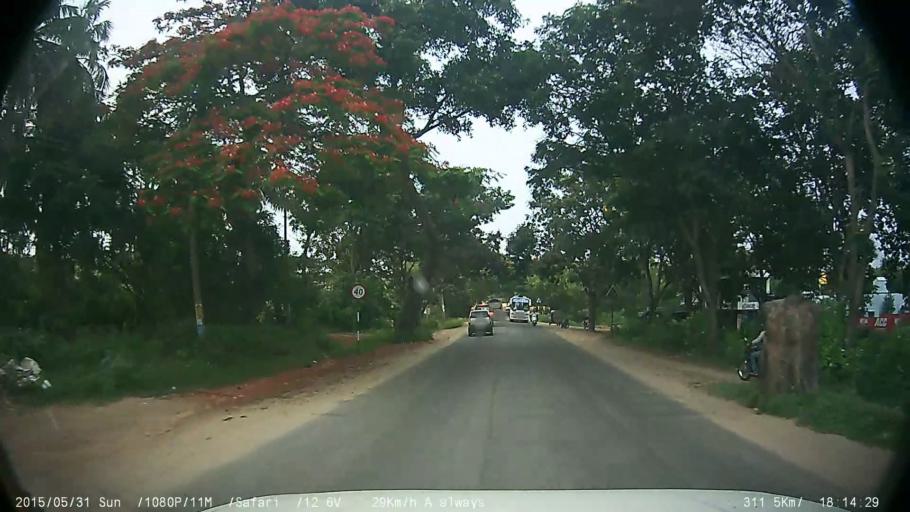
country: IN
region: Karnataka
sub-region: Mysore
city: Nanjangud
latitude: 12.1071
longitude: 76.6728
